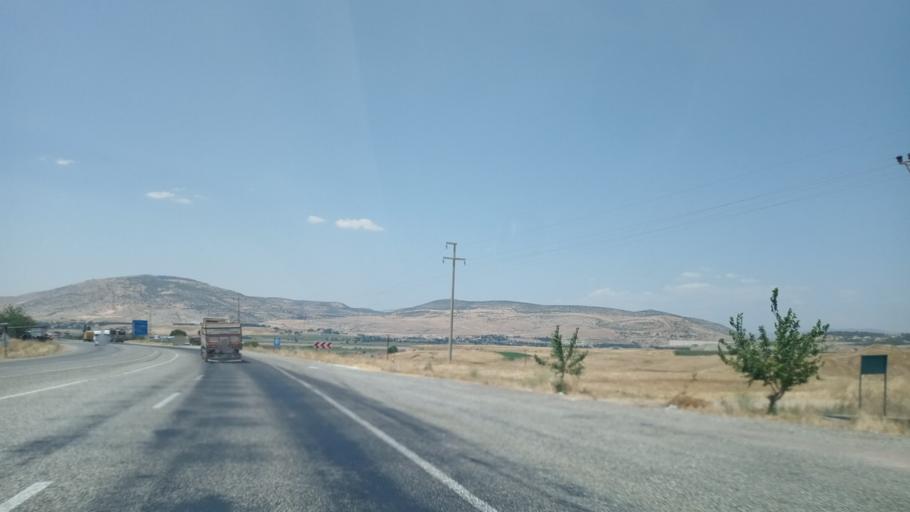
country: TR
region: Diyarbakir
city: Malabadi
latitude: 38.1350
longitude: 41.2352
